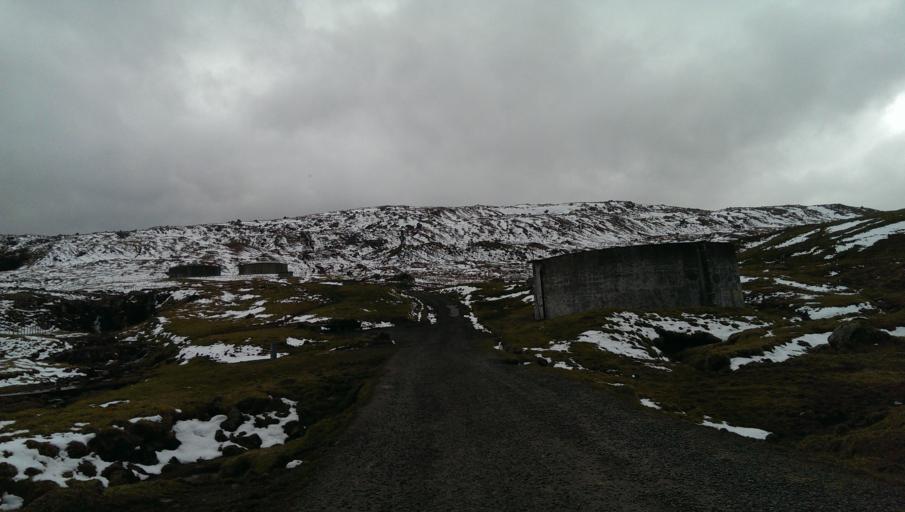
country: FO
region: Streymoy
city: Hoyvik
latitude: 62.0332
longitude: -6.8032
